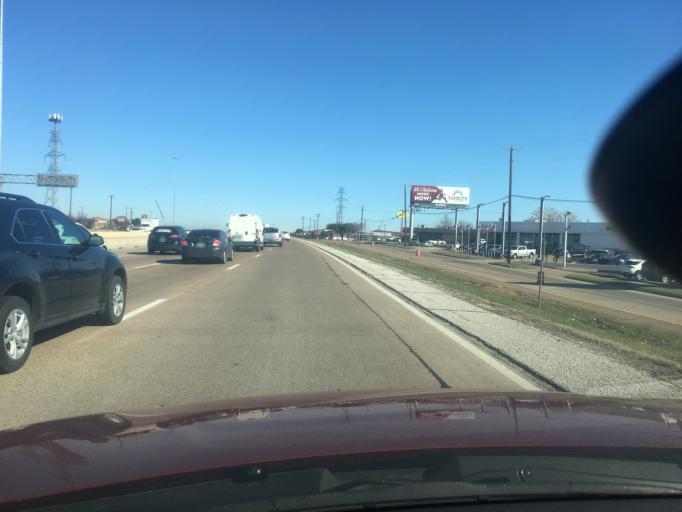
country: US
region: Texas
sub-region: Dallas County
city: Cockrell Hill
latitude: 32.6996
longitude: -96.8375
